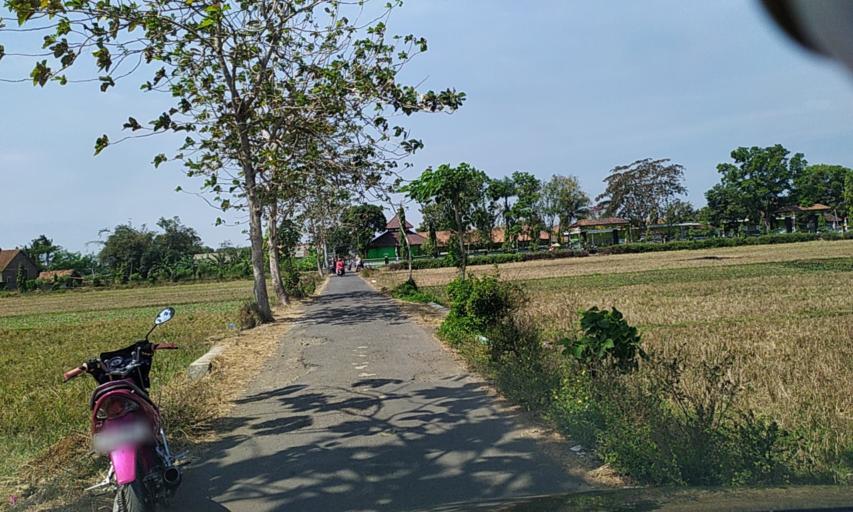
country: ID
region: Central Java
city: Rejanegara
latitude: -7.6736
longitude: 109.0587
